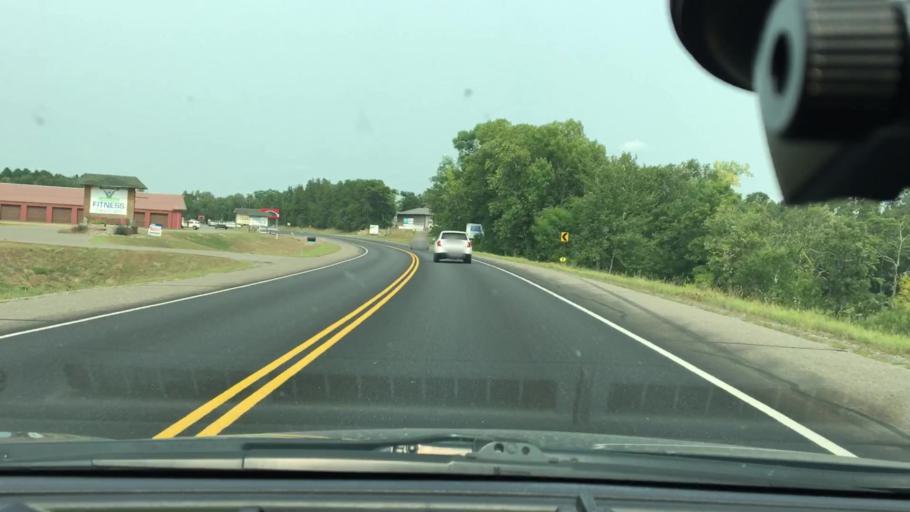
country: US
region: Minnesota
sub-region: Crow Wing County
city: Cross Lake
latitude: 46.6384
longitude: -94.1159
